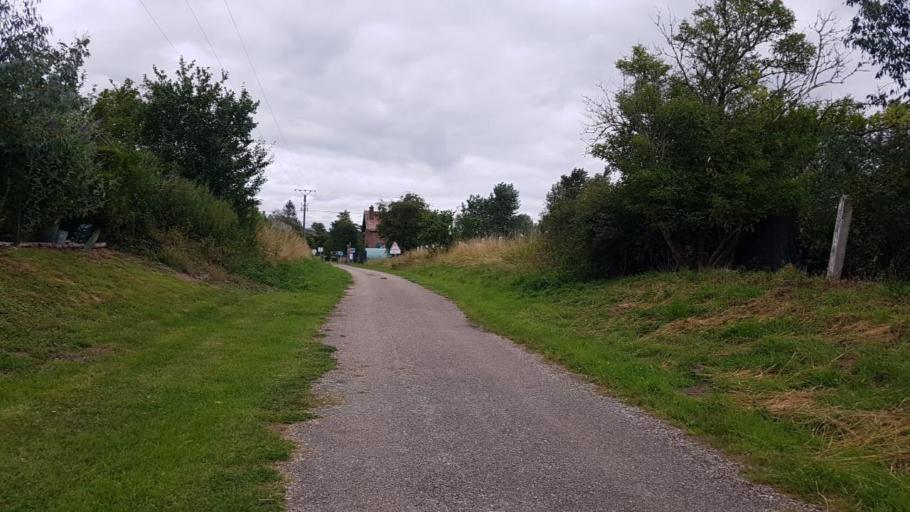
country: FR
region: Picardie
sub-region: Departement de l'Aisne
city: Origny-en-Thierache
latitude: 49.9235
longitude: 3.9625
